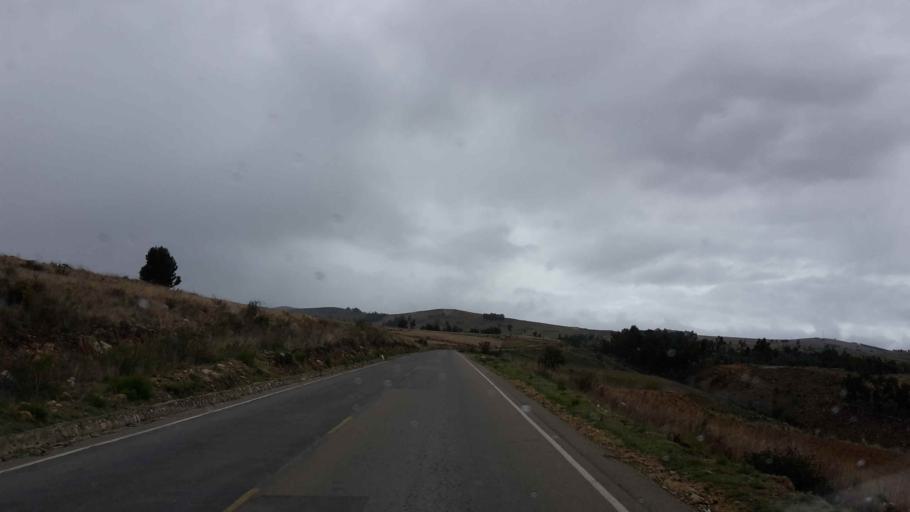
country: BO
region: Cochabamba
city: Arani
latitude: -17.4643
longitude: -65.6917
